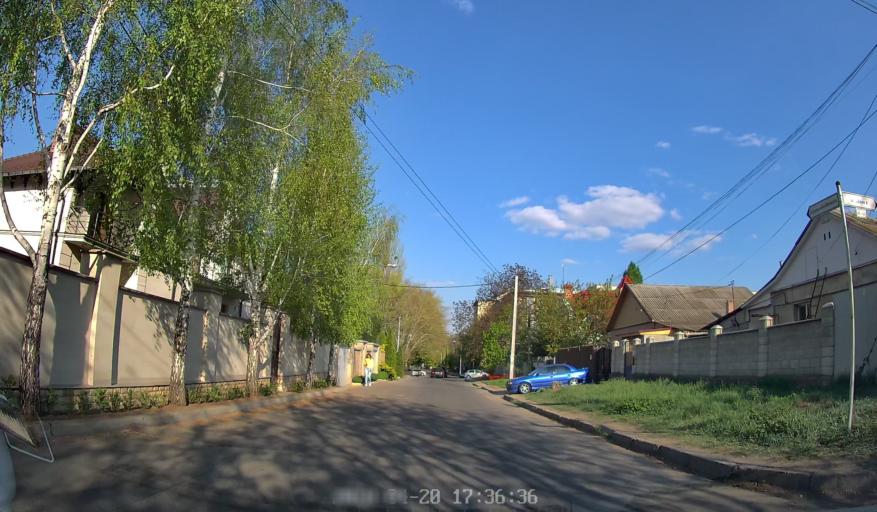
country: MD
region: Chisinau
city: Chisinau
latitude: 46.9888
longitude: 28.8637
